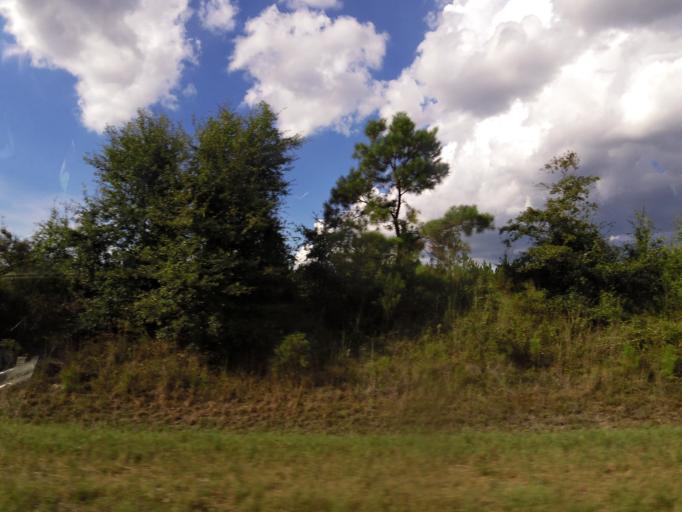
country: US
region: Georgia
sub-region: Brooks County
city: Quitman
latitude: 30.7952
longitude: -83.4323
